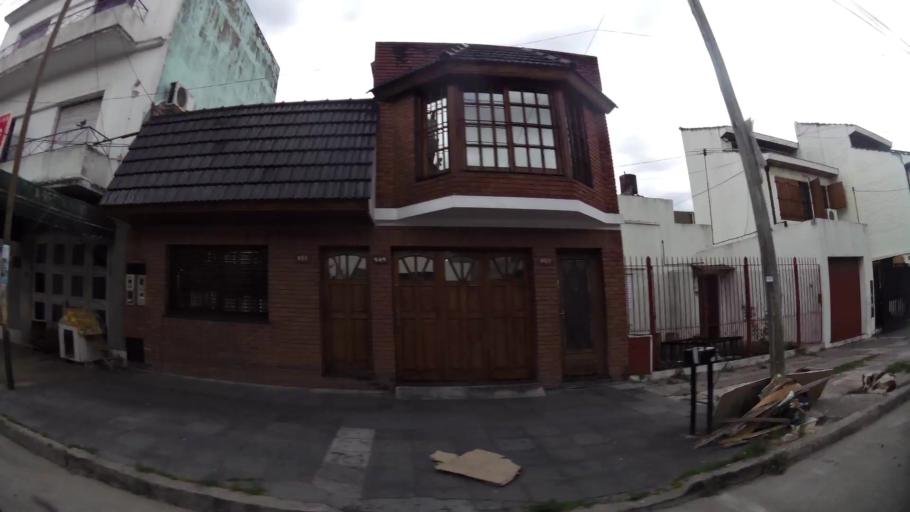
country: AR
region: Buenos Aires
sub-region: Partido de Lanus
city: Lanus
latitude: -34.6857
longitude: -58.3888
